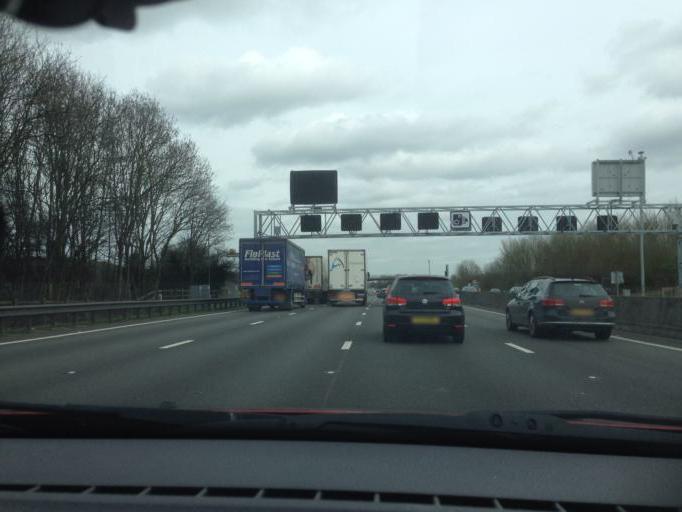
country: GB
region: England
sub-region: Kent
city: Westerham
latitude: 51.2768
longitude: 0.0794
